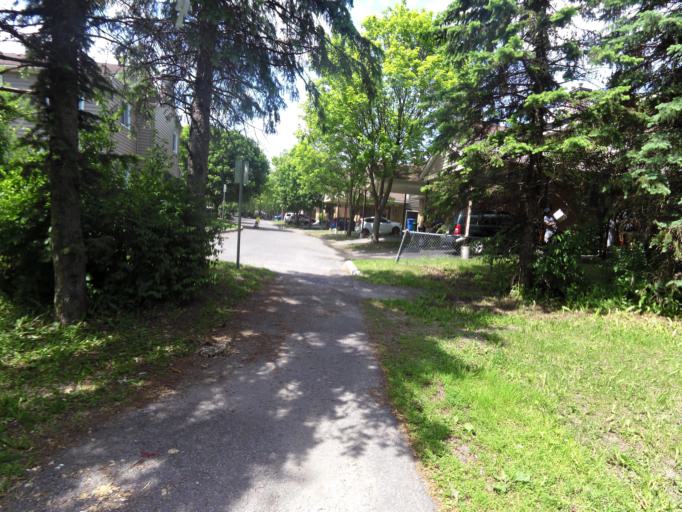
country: CA
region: Ontario
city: Ottawa
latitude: 45.3585
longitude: -75.6409
